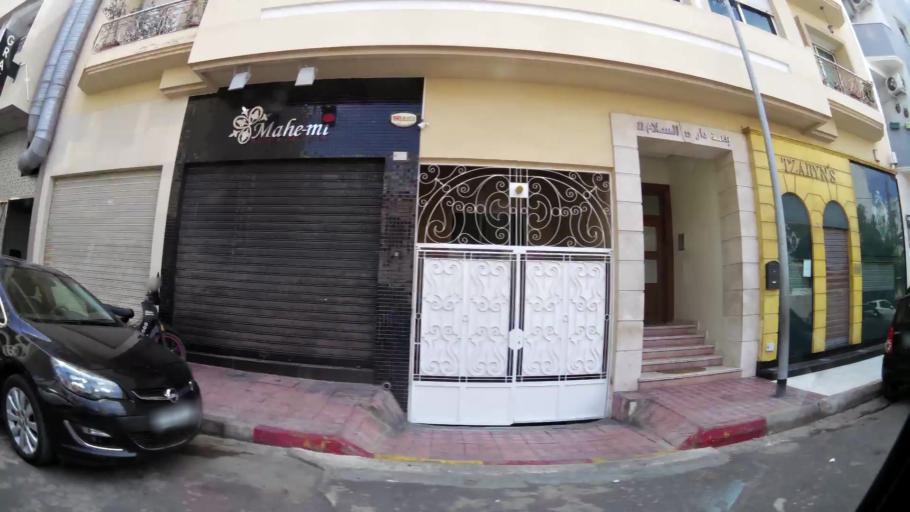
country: MA
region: Grand Casablanca
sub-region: Casablanca
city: Casablanca
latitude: 33.5934
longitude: -7.6409
